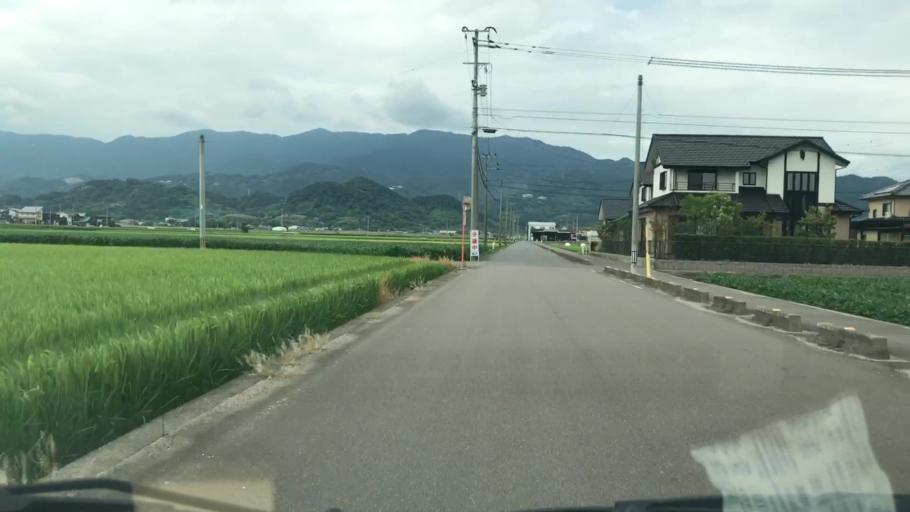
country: JP
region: Saga Prefecture
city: Saga-shi
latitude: 33.2853
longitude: 130.2254
